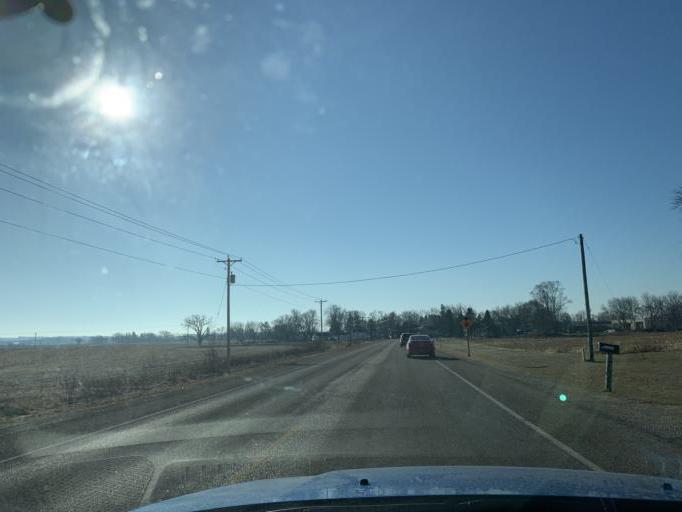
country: US
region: Wisconsin
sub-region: Dane County
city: Fitchburg
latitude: 42.9318
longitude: -89.5210
